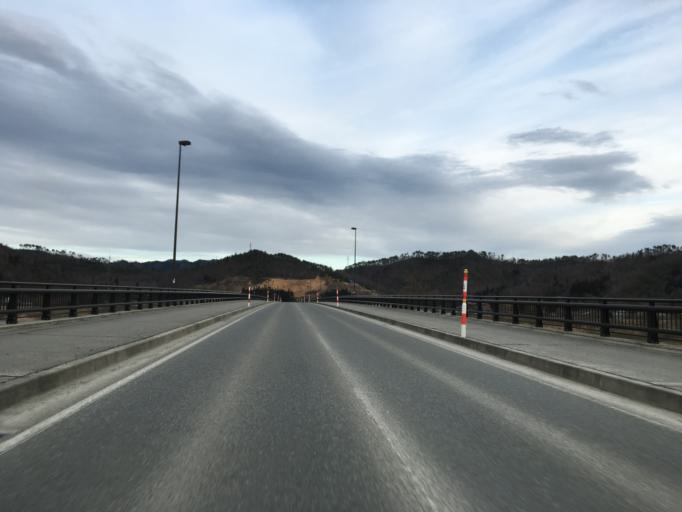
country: JP
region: Yamagata
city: Nagai
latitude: 38.0956
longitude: 140.0439
